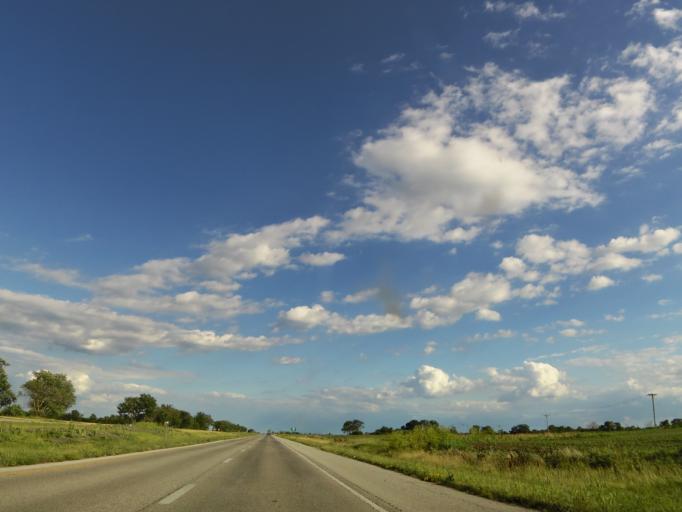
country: US
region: Missouri
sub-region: Lincoln County
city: Troy
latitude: 39.1955
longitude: -90.9959
